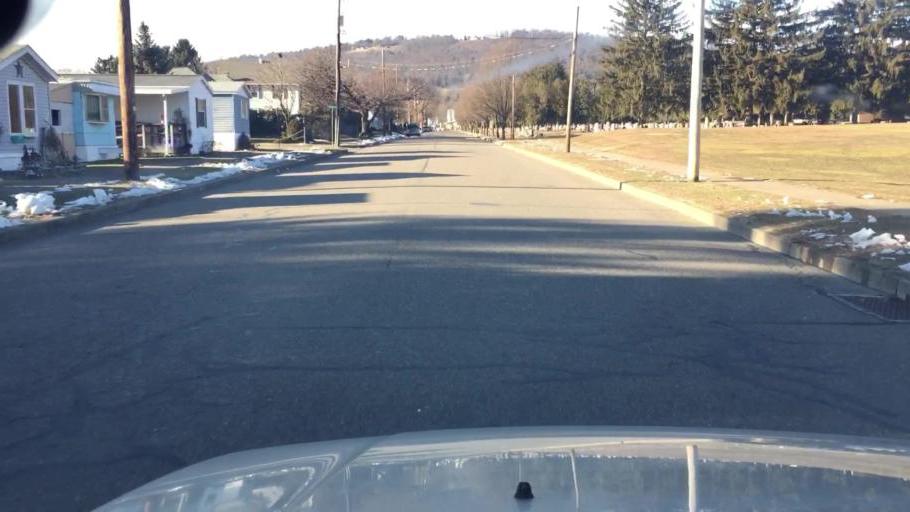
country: US
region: Pennsylvania
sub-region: Columbia County
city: Berwick
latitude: 41.0652
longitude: -76.2352
